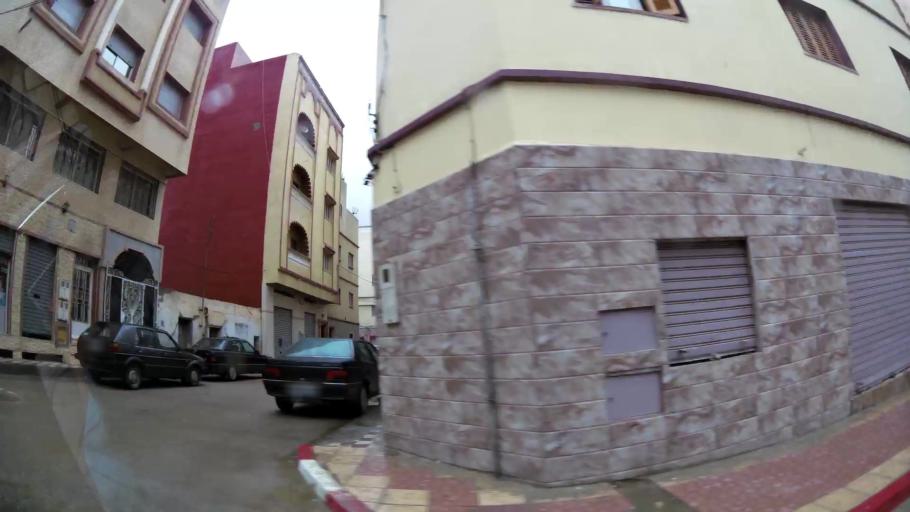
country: MA
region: Taza-Al Hoceima-Taounate
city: Al Hoceima
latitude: 35.2498
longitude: -3.9338
